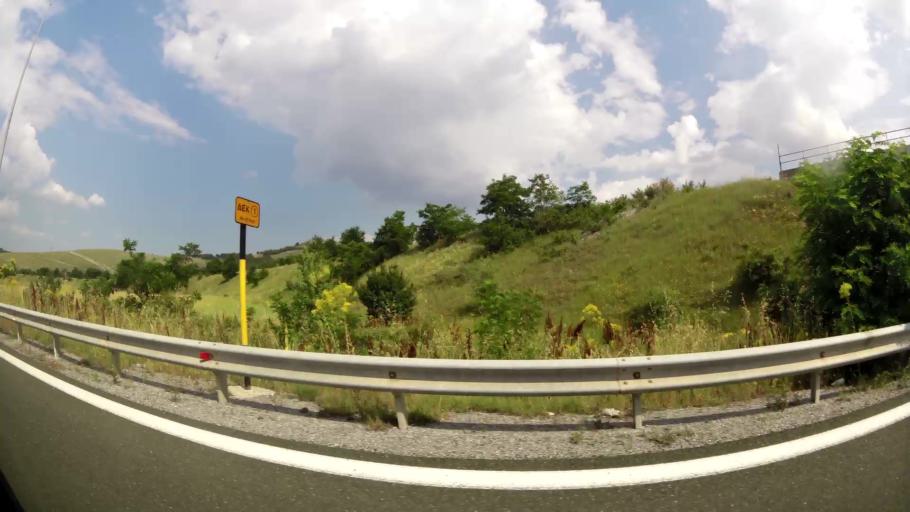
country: GR
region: West Macedonia
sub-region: Nomos Kozanis
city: Koila
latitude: 40.3507
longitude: 21.8086
